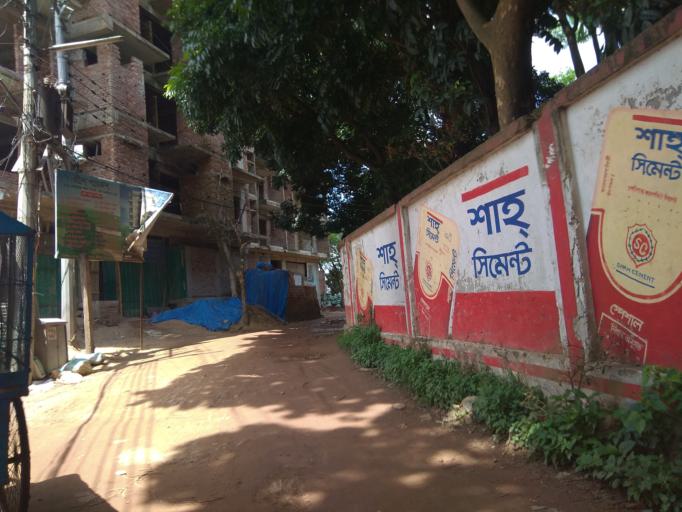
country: BD
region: Dhaka
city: Tungi
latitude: 23.8265
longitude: 90.3867
